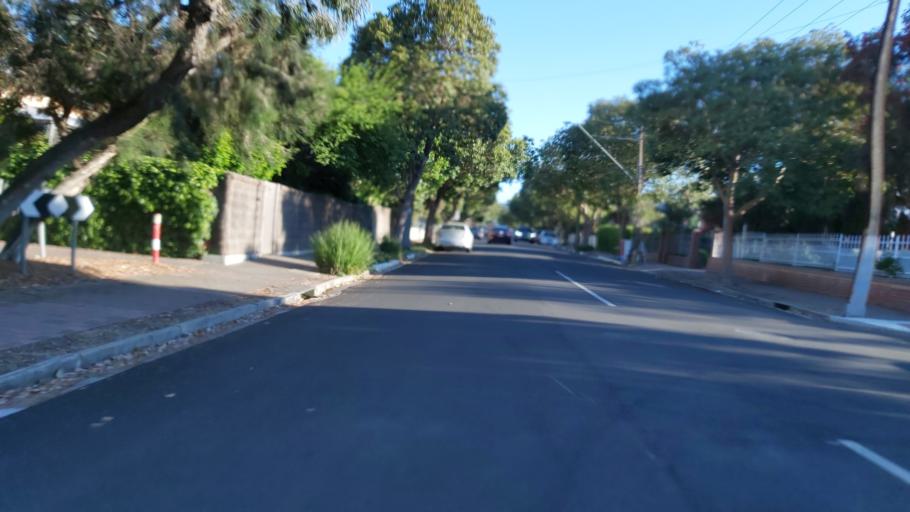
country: AU
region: South Australia
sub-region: Unley
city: Fullarton
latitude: -34.9513
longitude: 138.6216
